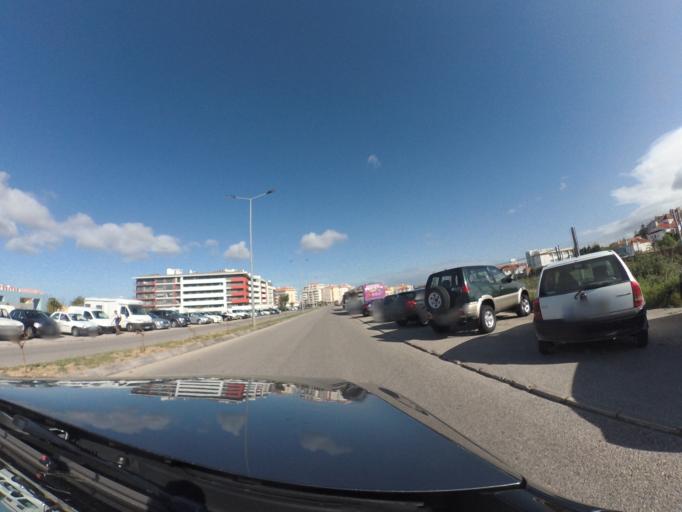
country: PT
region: Leiria
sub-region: Caldas da Rainha
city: Caldas da Rainha
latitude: 39.4108
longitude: -9.1354
